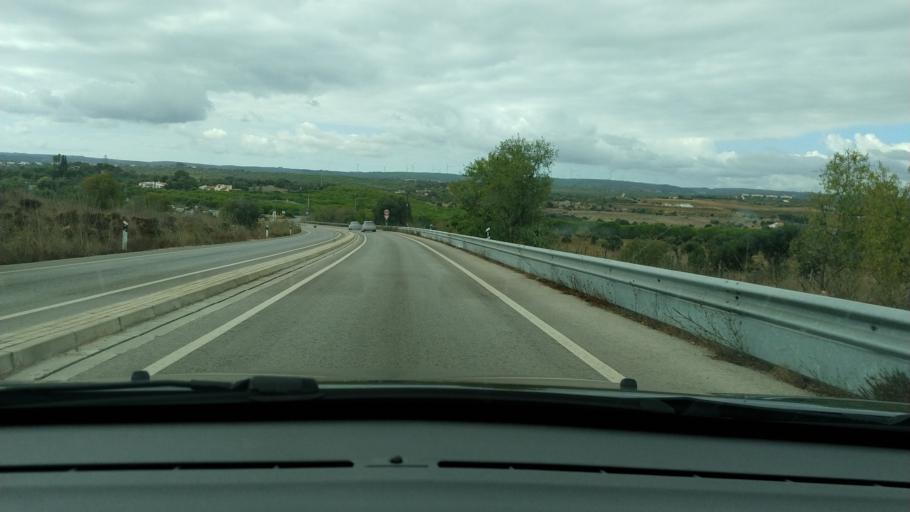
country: PT
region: Faro
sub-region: Lagos
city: Lagos
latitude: 37.0988
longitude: -8.7455
